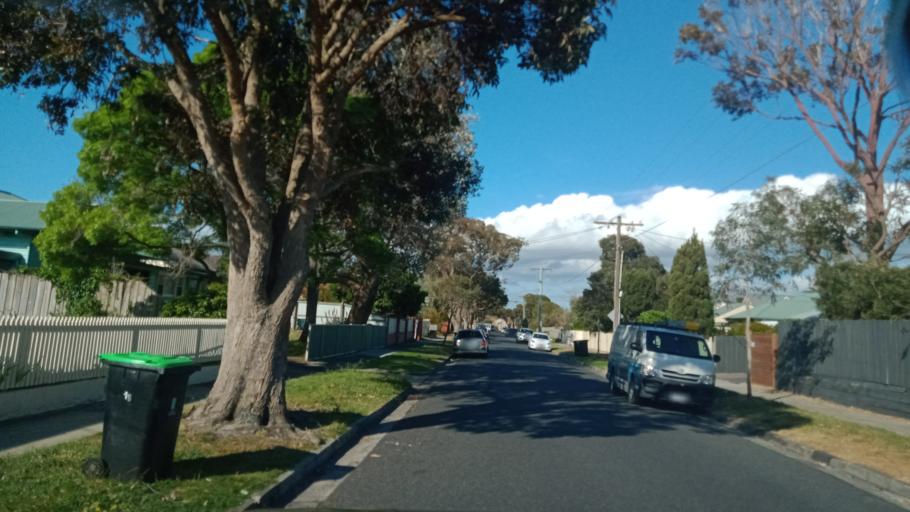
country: AU
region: Victoria
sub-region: Kingston
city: Chelsea
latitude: -38.0466
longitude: 145.1162
